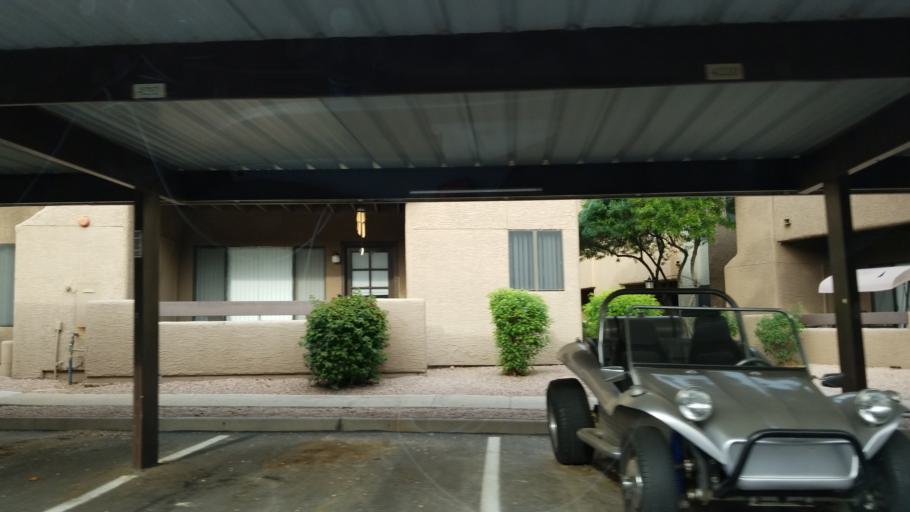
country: US
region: Arizona
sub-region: Maricopa County
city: Paradise Valley
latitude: 33.5776
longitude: -111.9294
